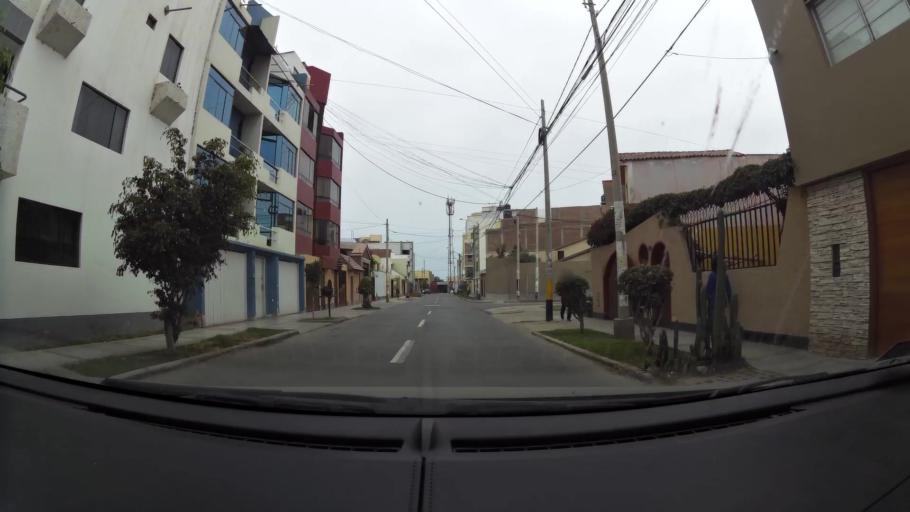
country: PE
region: La Libertad
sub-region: Provincia de Trujillo
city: Buenos Aires
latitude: -8.1348
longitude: -79.0410
